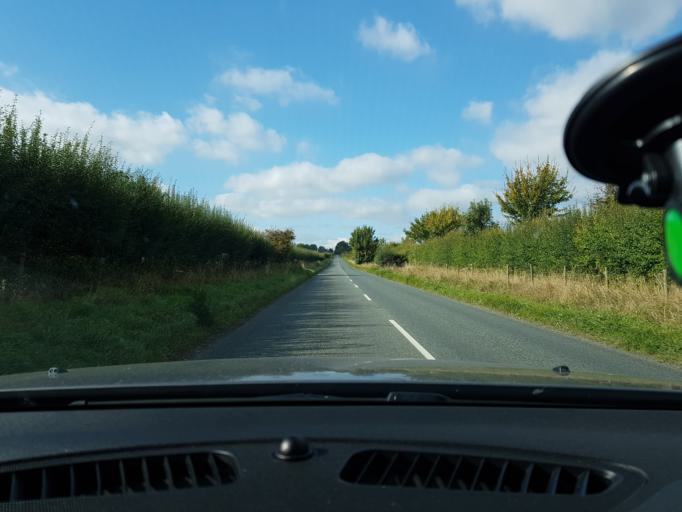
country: GB
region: England
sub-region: Wiltshire
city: Aldbourne
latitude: 51.4914
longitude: -1.6457
